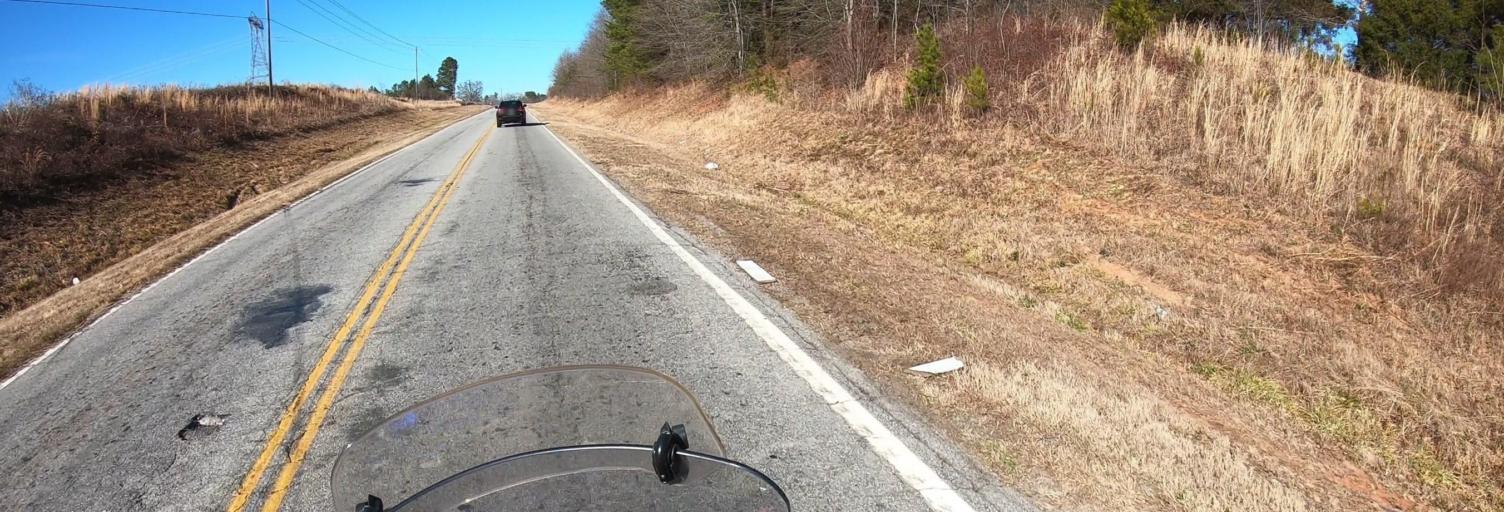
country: US
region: South Carolina
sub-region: Oconee County
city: Walhalla
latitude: 34.7283
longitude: -83.0606
